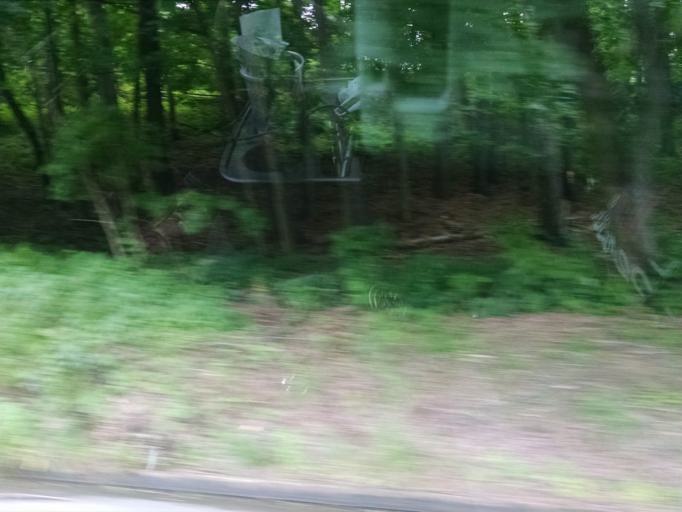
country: US
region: Pennsylvania
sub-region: Indiana County
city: Chevy Chase Heights
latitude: 40.6328
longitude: -79.1410
